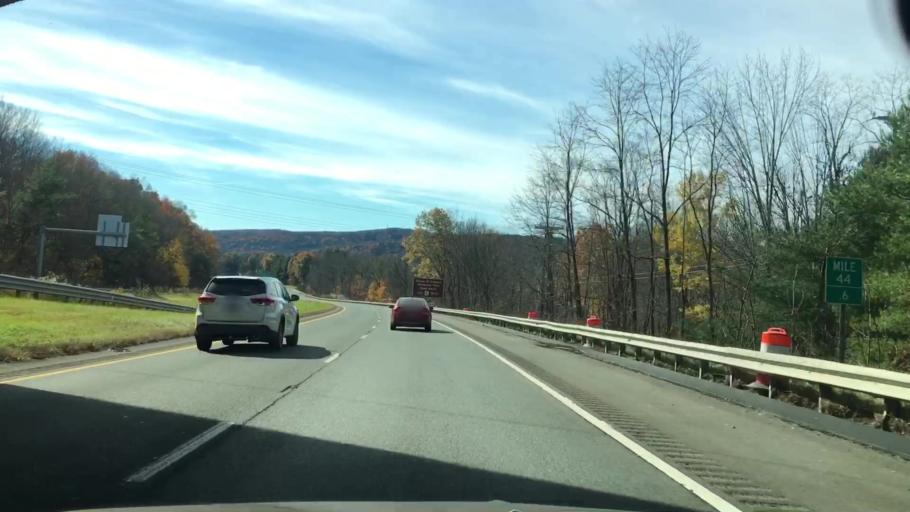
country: US
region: Massachusetts
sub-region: Franklin County
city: Greenfield
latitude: 42.6070
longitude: -72.6122
